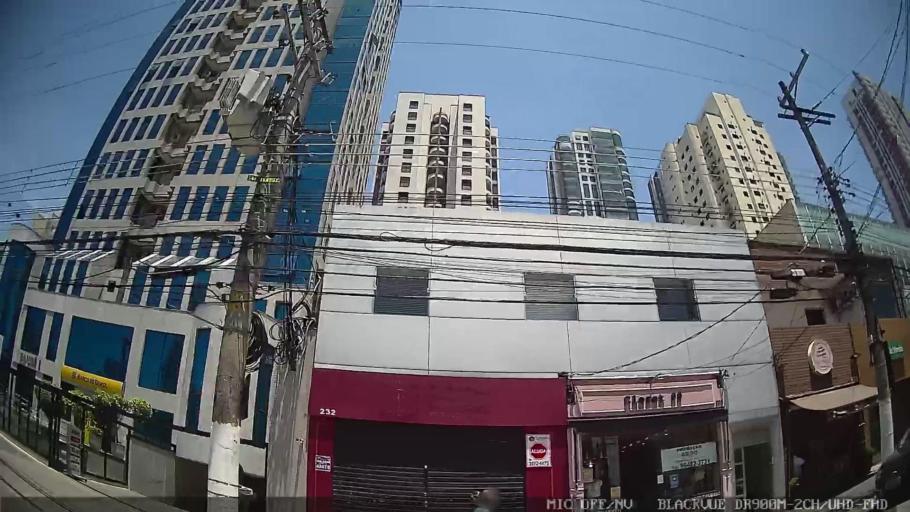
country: BR
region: Sao Paulo
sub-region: Sao Paulo
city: Sao Paulo
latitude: -23.5530
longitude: -46.5650
